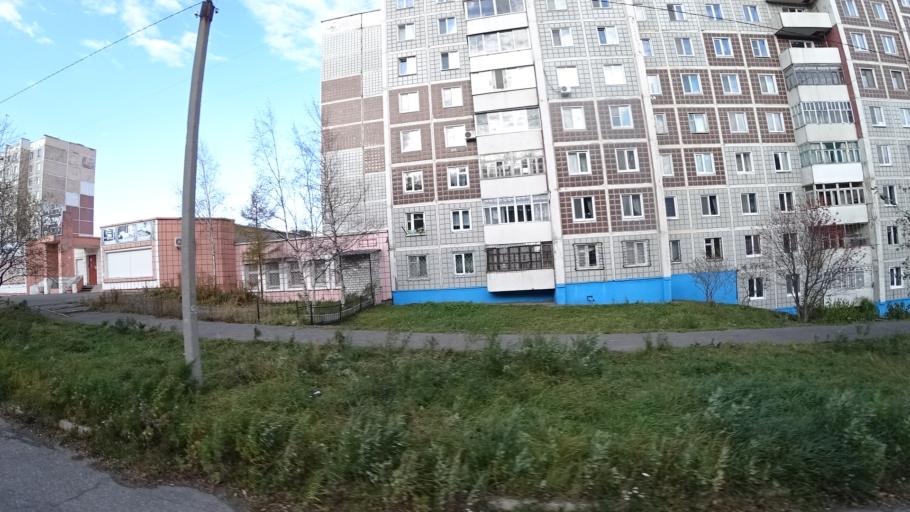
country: RU
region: Khabarovsk Krai
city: Amursk
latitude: 50.2463
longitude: 136.9218
